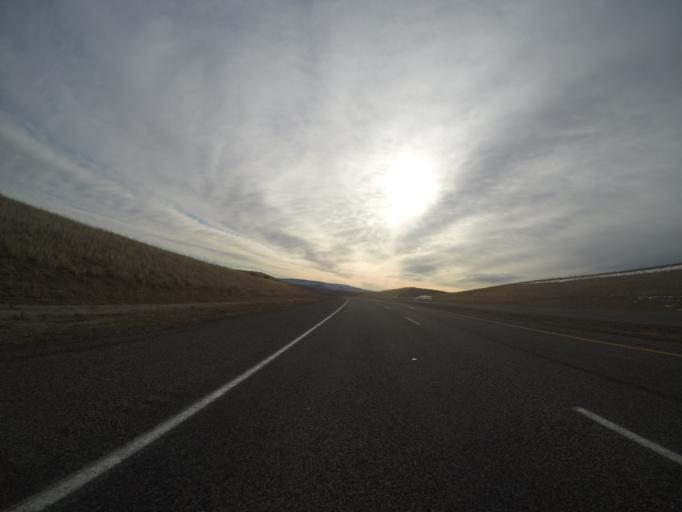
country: US
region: Montana
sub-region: Yellowstone County
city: Laurel
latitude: 45.5468
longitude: -108.8619
